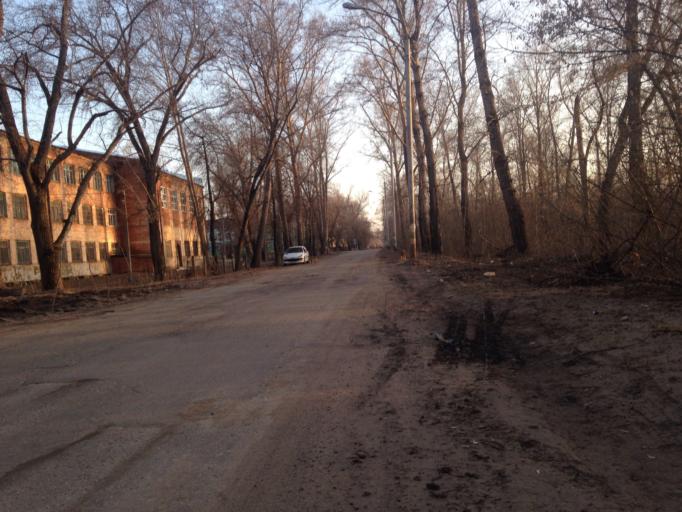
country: RU
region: Ulyanovsk
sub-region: Ulyanovskiy Rayon
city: Ulyanovsk
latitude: 54.3343
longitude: 48.4733
